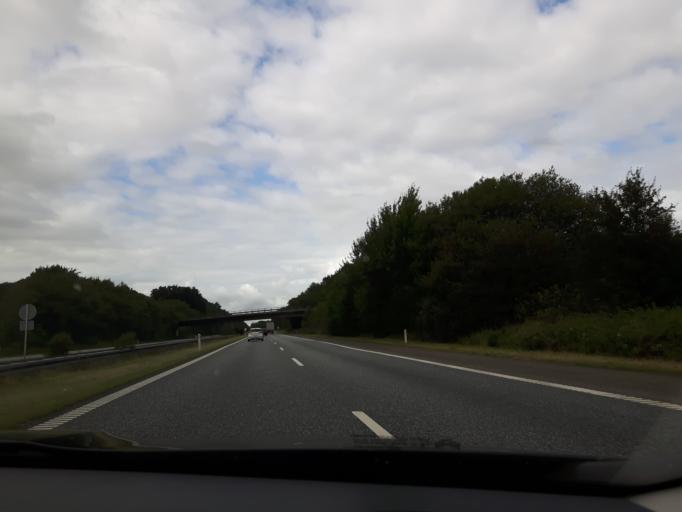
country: DK
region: South Denmark
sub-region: Aabenraa Kommune
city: Aabenraa
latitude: 54.9999
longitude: 9.3692
